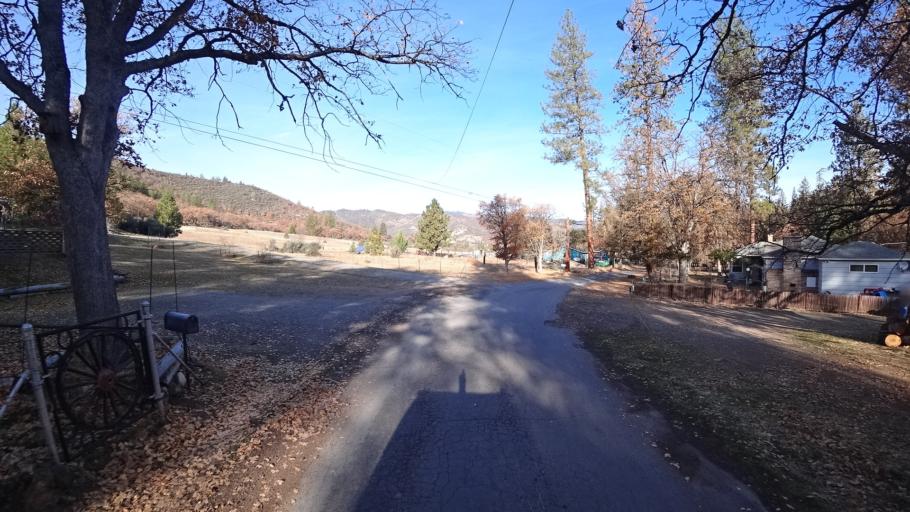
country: US
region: California
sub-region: Siskiyou County
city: Yreka
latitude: 41.6849
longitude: -122.6411
